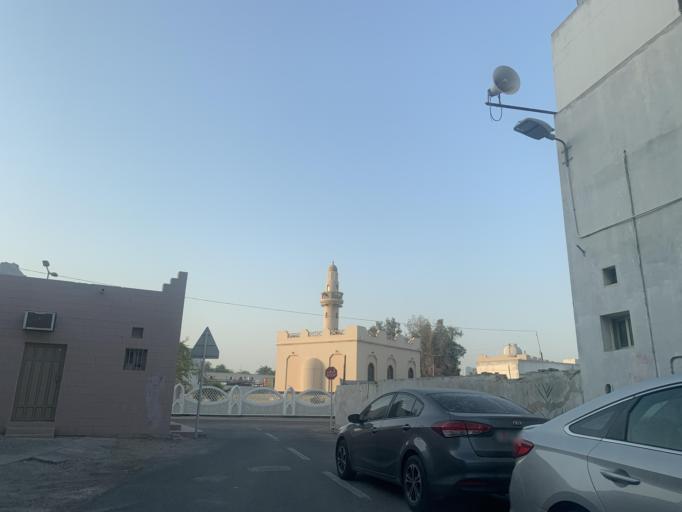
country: BH
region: Manama
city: Jidd Hafs
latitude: 26.2160
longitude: 50.5295
